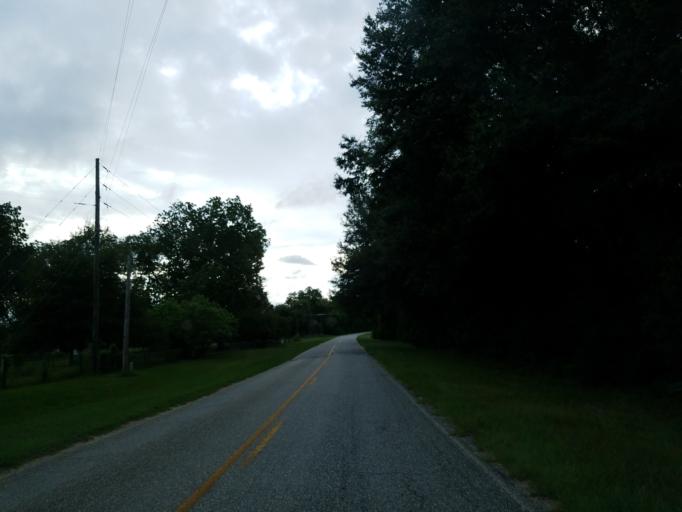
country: US
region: Georgia
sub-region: Cook County
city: Sparks
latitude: 31.2153
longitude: -83.4622
